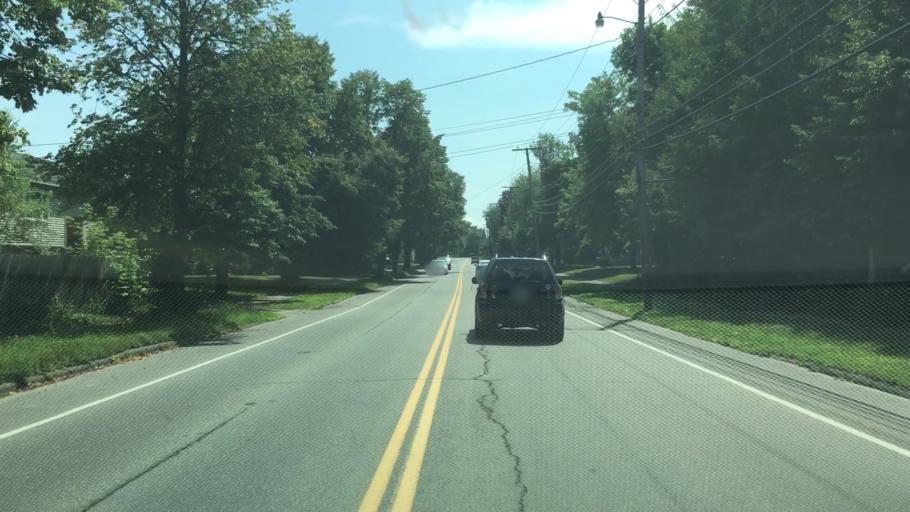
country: US
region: Maine
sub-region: Penobscot County
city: Brewer
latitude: 44.8191
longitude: -68.7630
